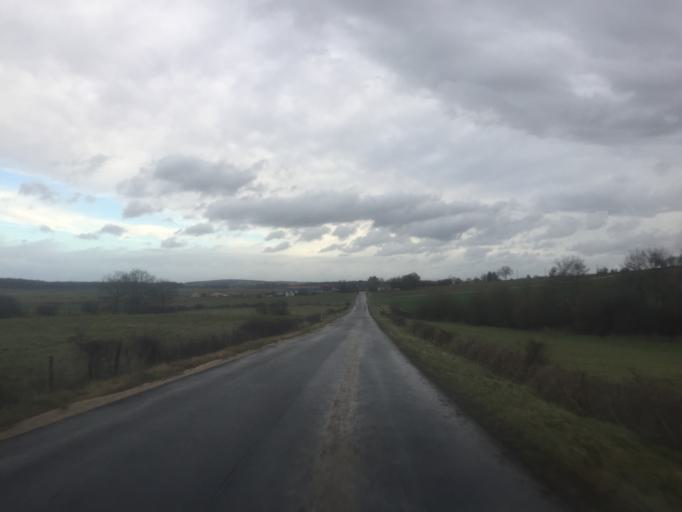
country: FR
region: Franche-Comte
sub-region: Departement de la Haute-Saone
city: Pesmes
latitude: 47.2263
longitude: 5.5518
